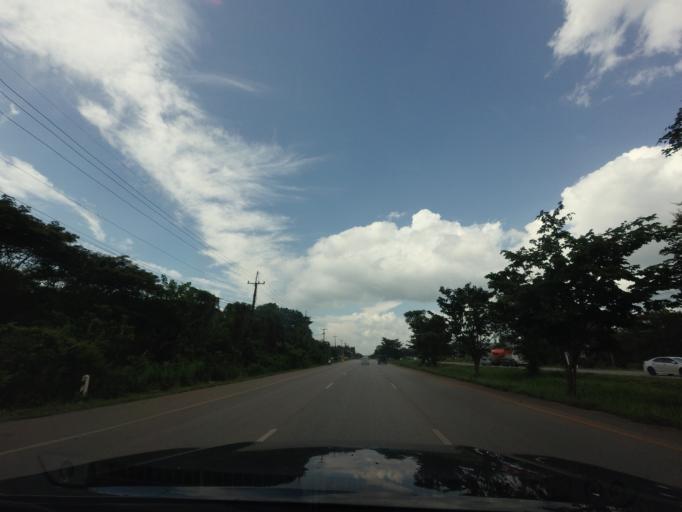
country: TH
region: Changwat Udon Thani
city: Udon Thani
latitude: 17.5381
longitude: 102.8001
